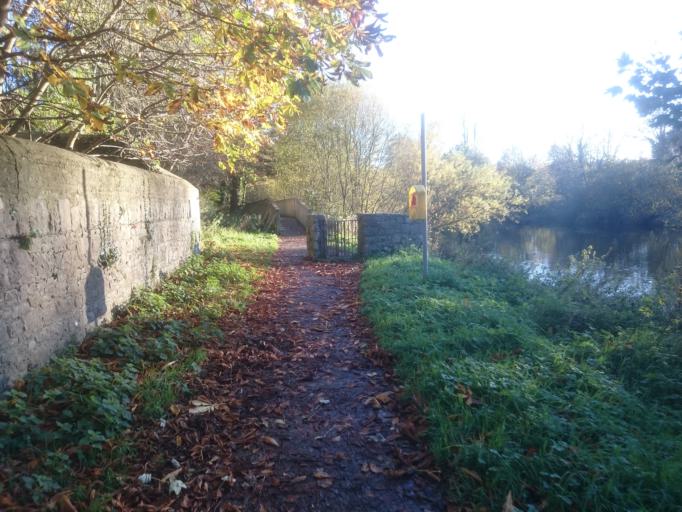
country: IE
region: Leinster
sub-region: Kilkenny
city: Kilkenny
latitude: 52.6462
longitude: -7.2348
